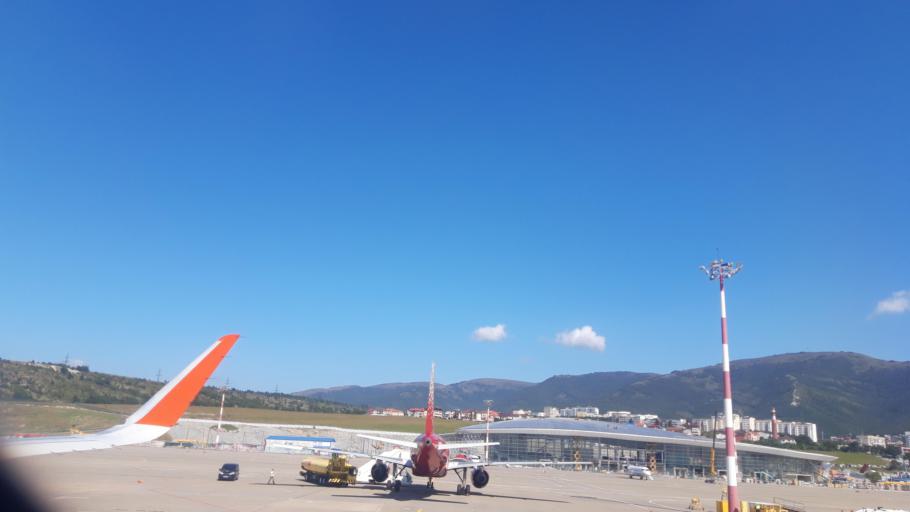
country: RU
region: Krasnodarskiy
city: Gelendzhik
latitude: 44.5923
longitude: 38.0216
